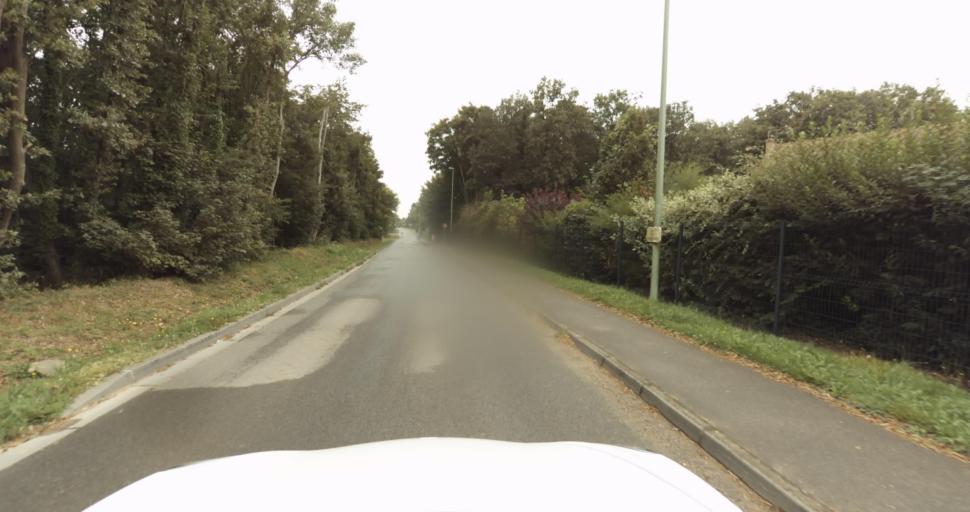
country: FR
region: Haute-Normandie
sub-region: Departement de l'Eure
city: Aviron
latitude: 49.0481
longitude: 1.1282
